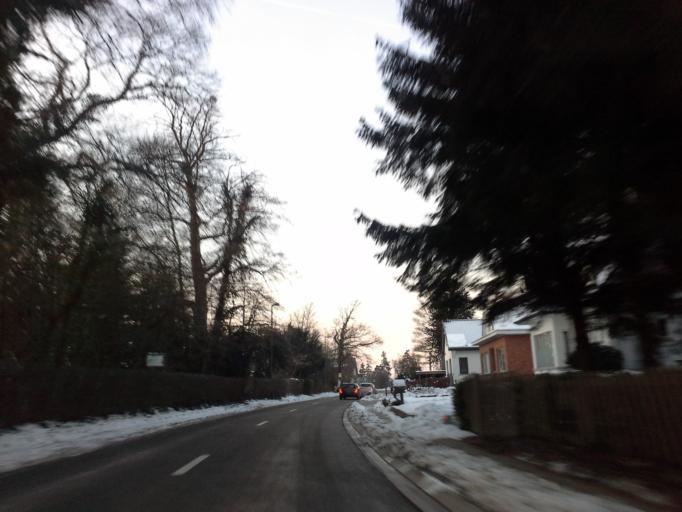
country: BE
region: Flanders
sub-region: Provincie Vlaams-Brabant
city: Lubbeek
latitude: 50.8672
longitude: 4.7947
